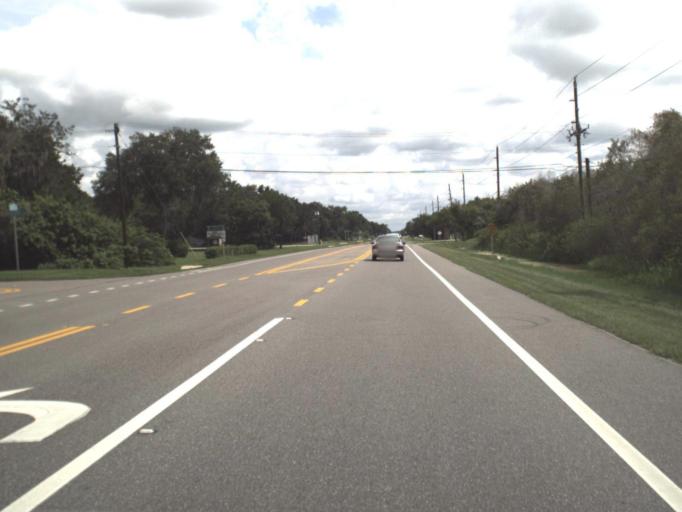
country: US
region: Florida
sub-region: Sarasota County
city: Lake Sarasota
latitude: 27.2664
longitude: -82.4152
